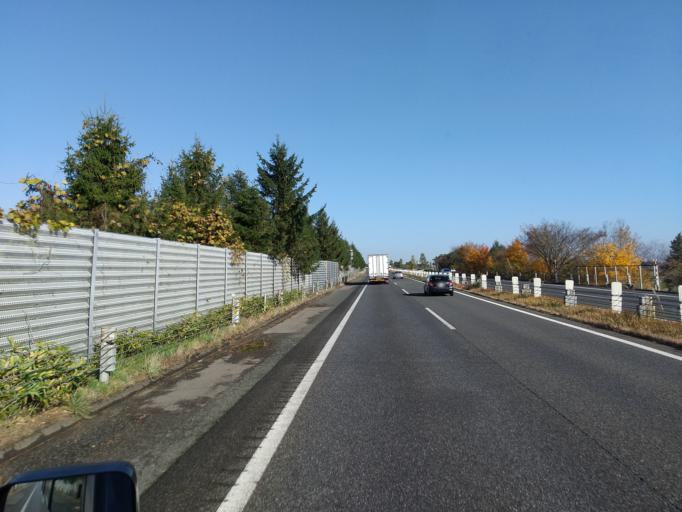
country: JP
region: Iwate
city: Hanamaki
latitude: 39.4740
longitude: 141.1094
